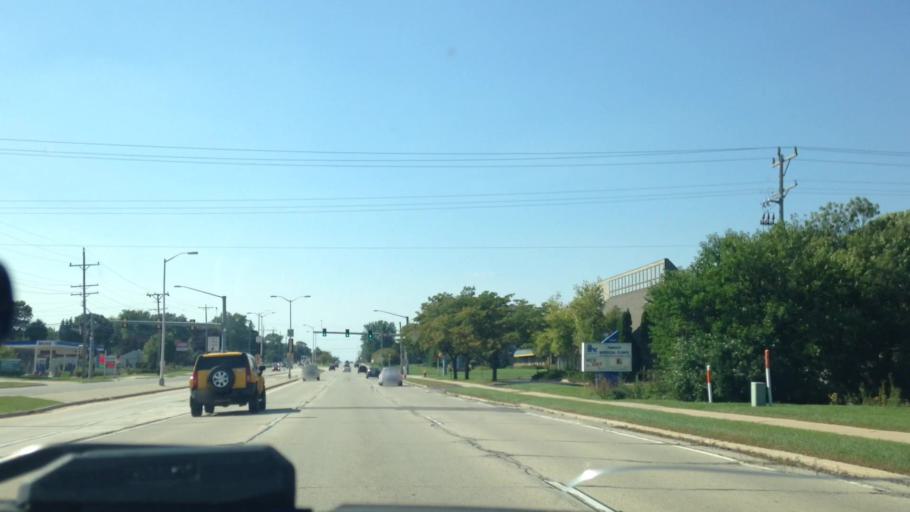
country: US
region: Wisconsin
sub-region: Milwaukee County
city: Brown Deer
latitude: 43.1778
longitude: -87.9725
